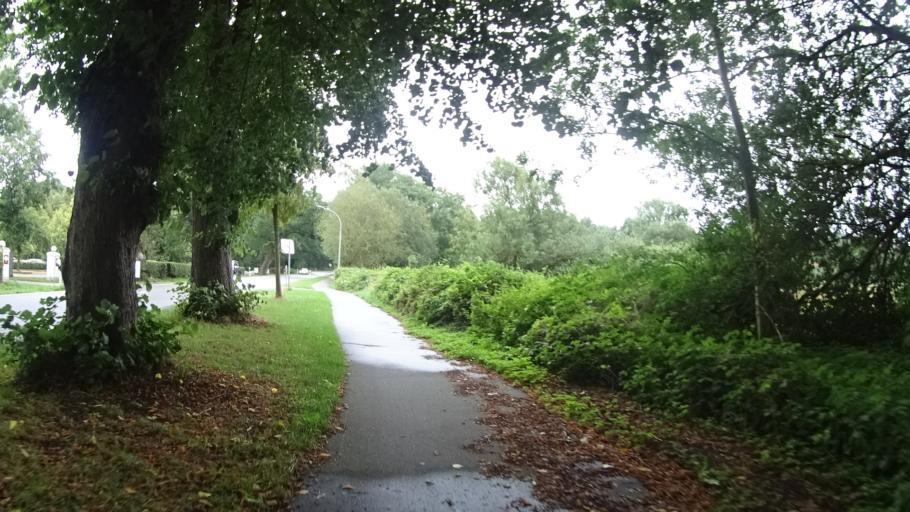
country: DE
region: Schleswig-Holstein
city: Alveslohe
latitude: 53.7847
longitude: 9.9452
